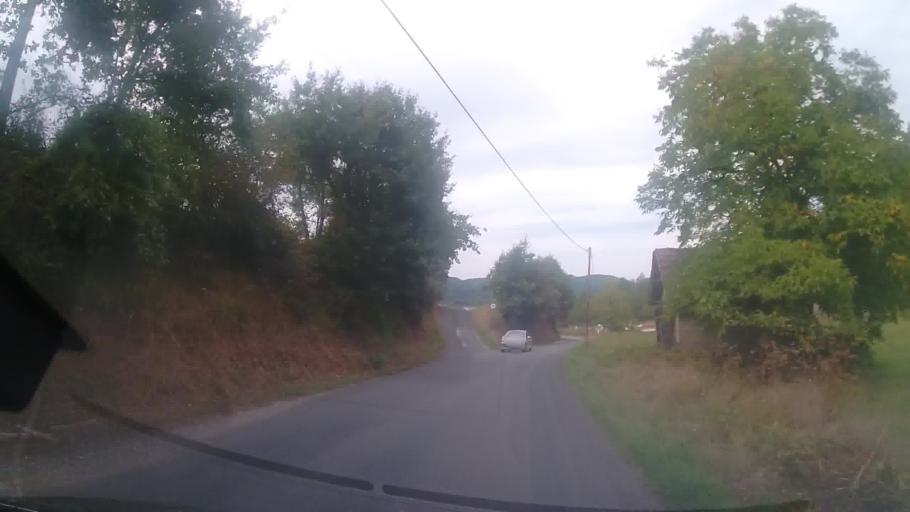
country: FR
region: Aquitaine
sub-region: Departement de la Dordogne
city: Eyvigues-et-Eybenes
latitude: 44.8490
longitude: 1.3649
